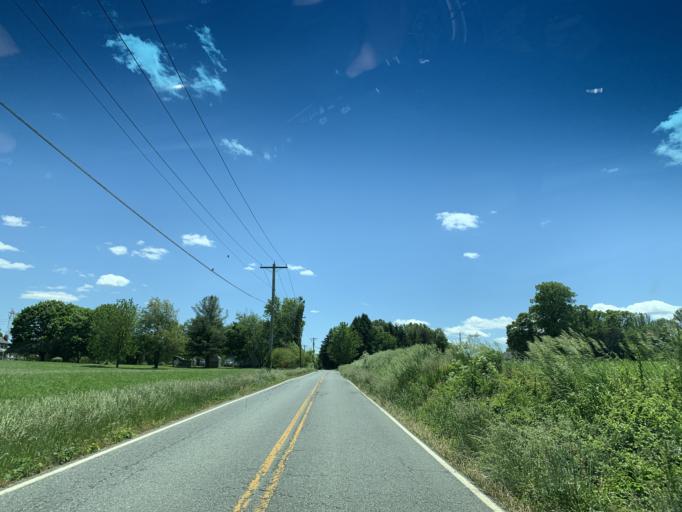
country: US
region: Maryland
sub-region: Cecil County
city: Rising Sun
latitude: 39.6741
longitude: -76.0180
